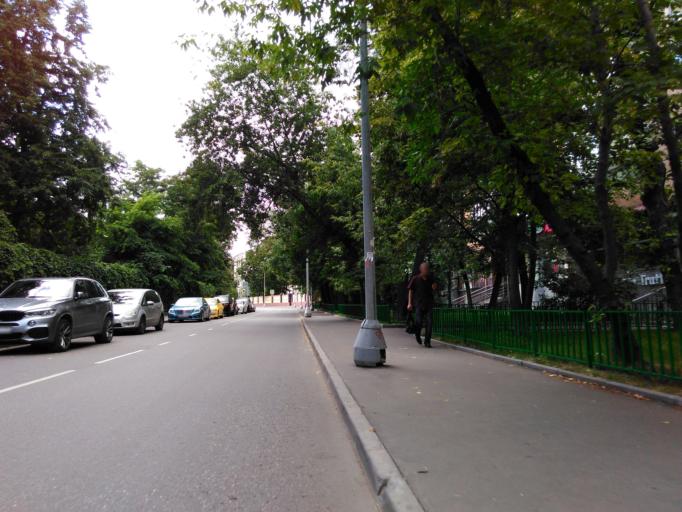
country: RU
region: Moskovskaya
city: Dorogomilovo
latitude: 55.7308
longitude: 37.5786
